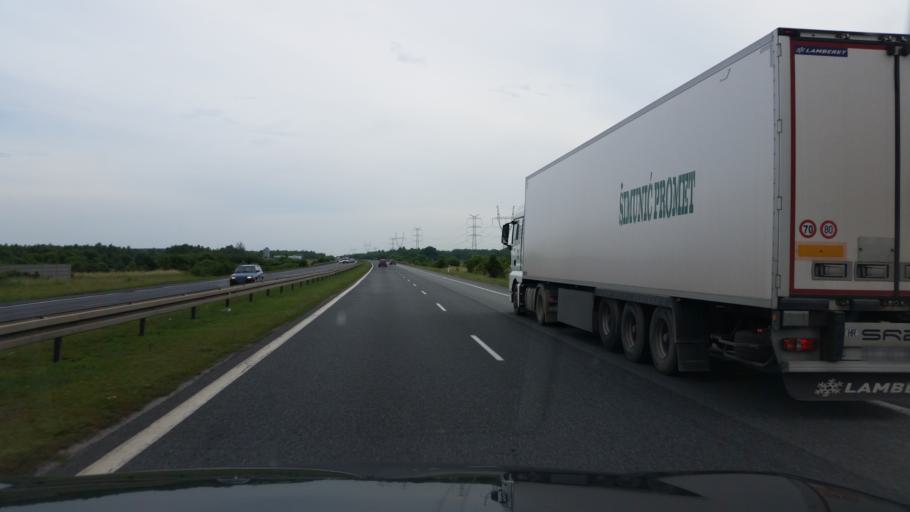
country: PL
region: Lodz Voivodeship
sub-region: Powiat radomszczanski
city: Radomsko
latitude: 51.1020
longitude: 19.3844
